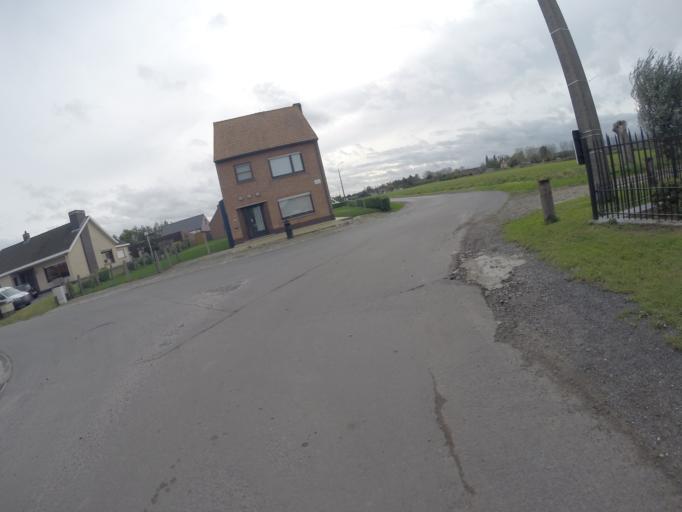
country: BE
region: Flanders
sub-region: Provincie Oost-Vlaanderen
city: Maldegem
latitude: 51.1857
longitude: 3.4401
